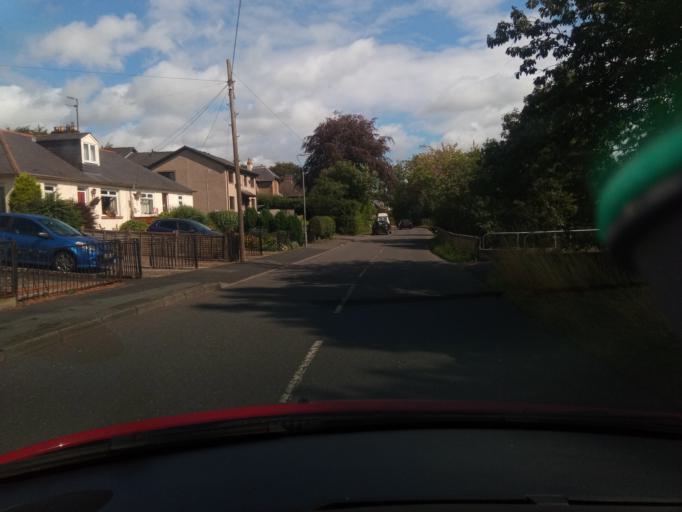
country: GB
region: Scotland
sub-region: The Scottish Borders
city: Melrose
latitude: 55.5926
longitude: -2.7250
